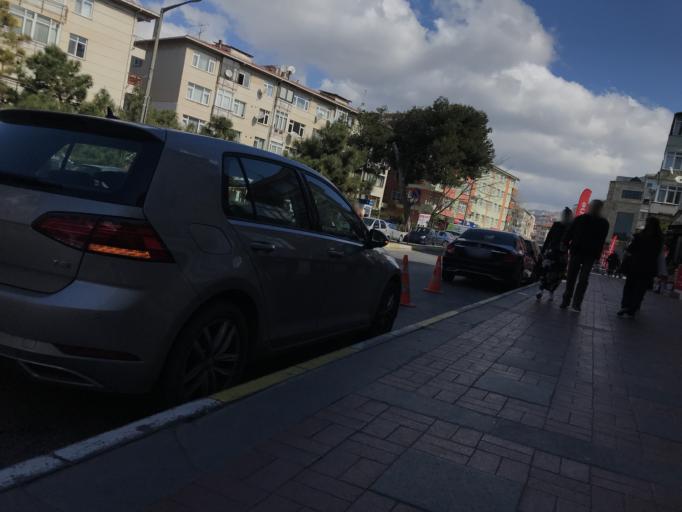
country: TR
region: Istanbul
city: Maltepe
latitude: 40.9263
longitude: 29.1328
